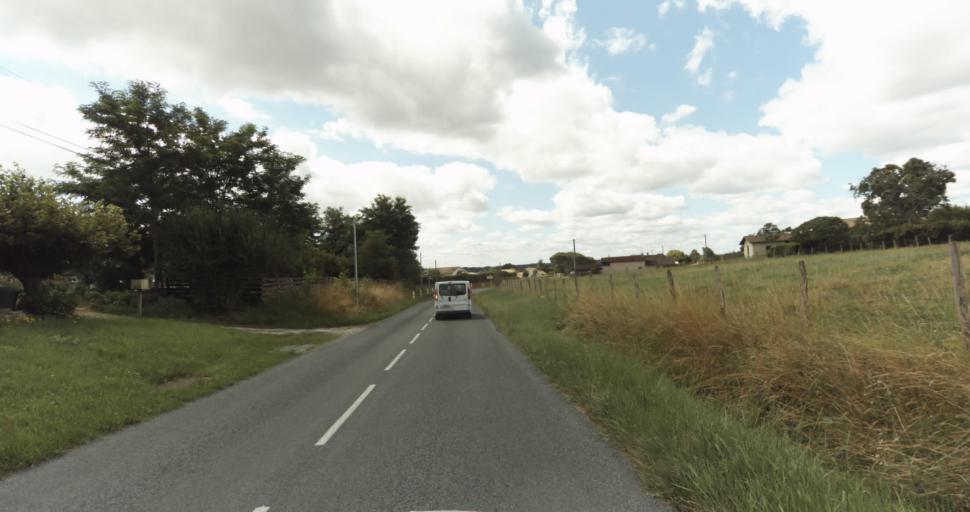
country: FR
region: Aquitaine
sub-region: Departement de la Gironde
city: Bazas
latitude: 44.4418
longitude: -0.2064
